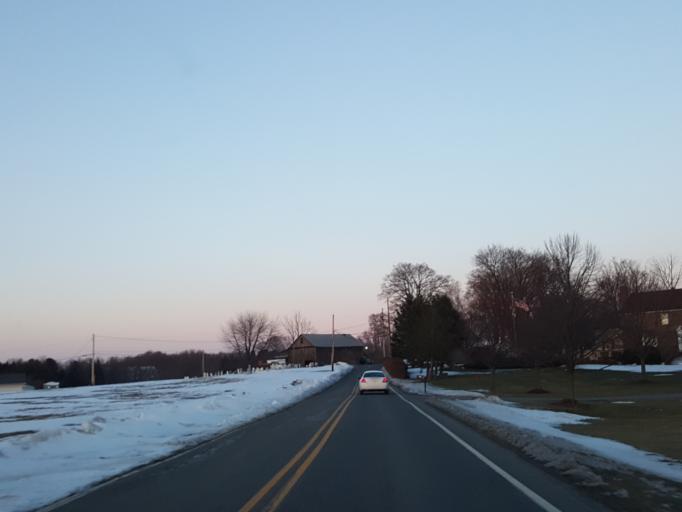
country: US
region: Pennsylvania
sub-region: Dauphin County
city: Hummelstown
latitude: 40.2857
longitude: -76.7275
